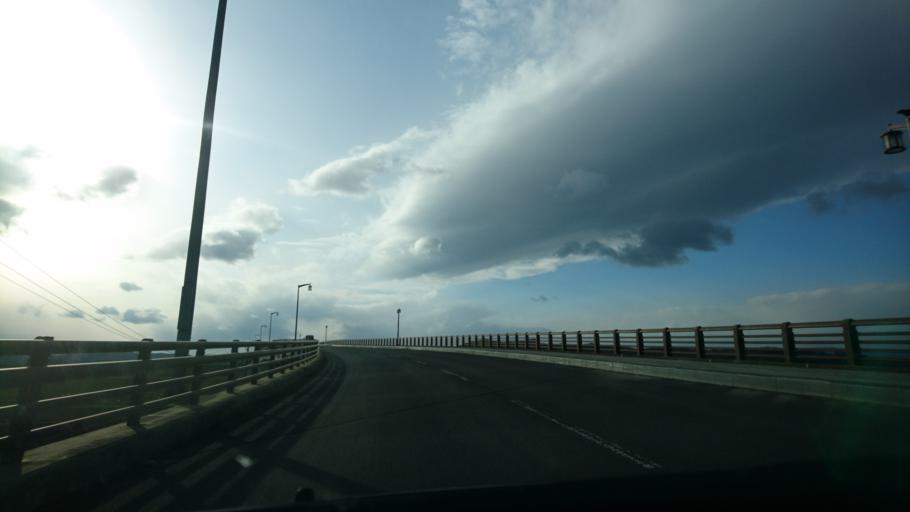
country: JP
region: Iwate
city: Ichinoseki
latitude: 38.9935
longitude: 141.1284
